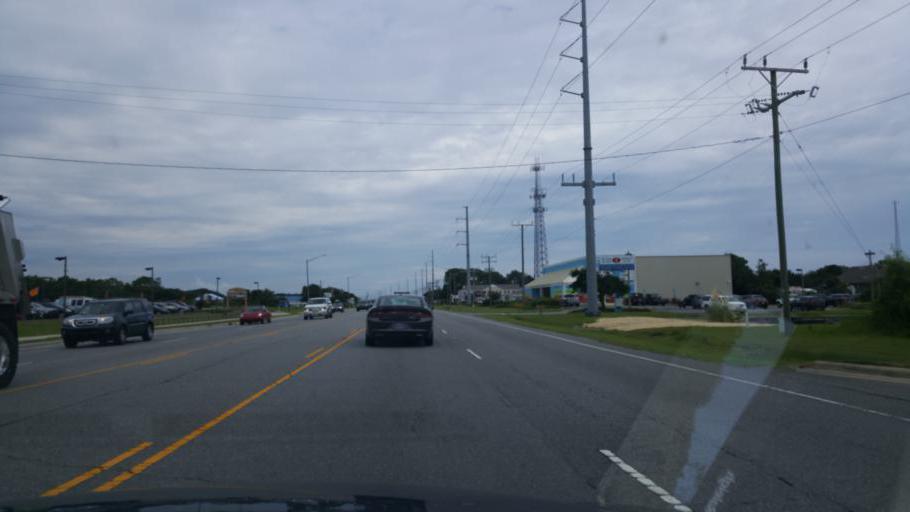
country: US
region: North Carolina
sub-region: Dare County
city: Nags Head
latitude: 35.9855
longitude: -75.6446
